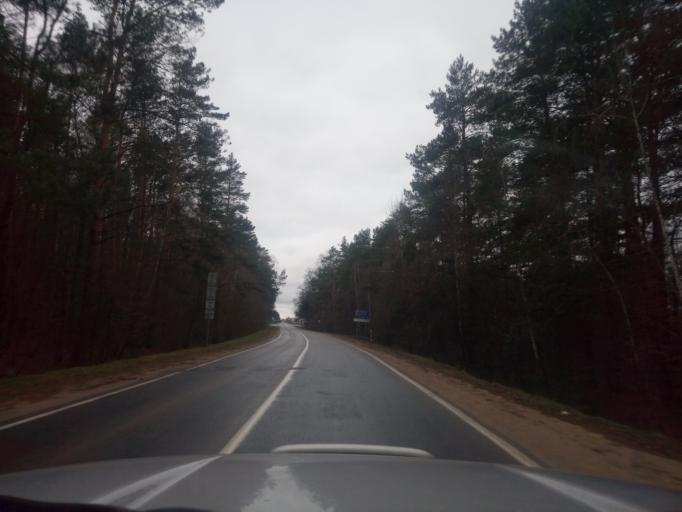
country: BY
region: Minsk
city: Kapyl'
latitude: 53.1587
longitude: 27.1077
